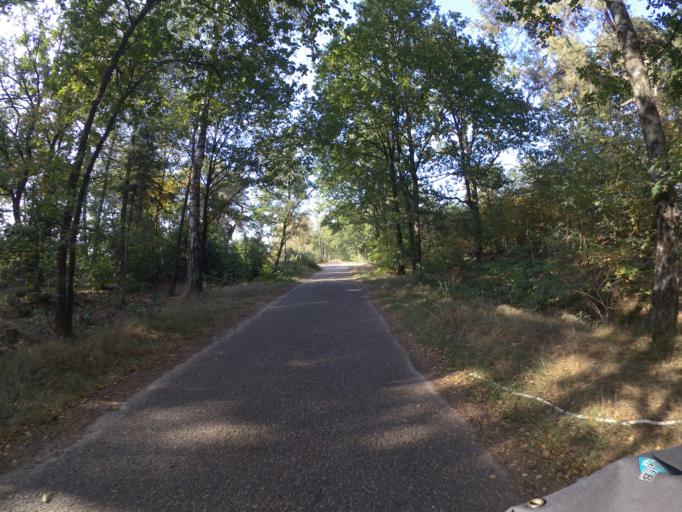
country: NL
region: North Brabant
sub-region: Gemeente Oirschot
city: Oirschot
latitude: 51.4772
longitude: 5.3272
